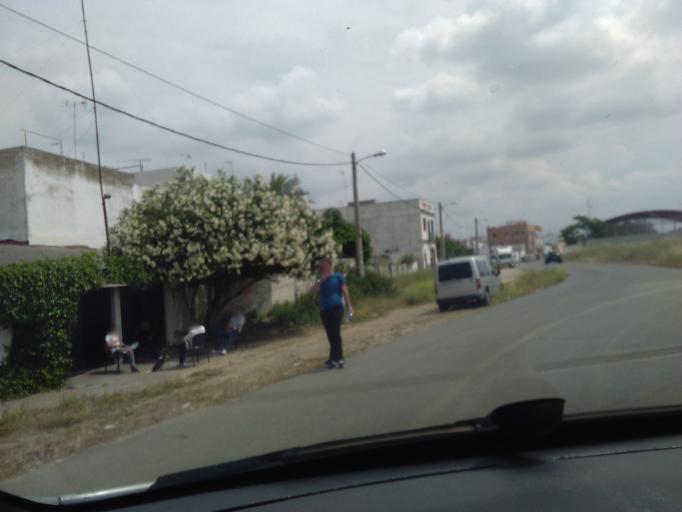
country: ES
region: Andalusia
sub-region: Provincia de Sevilla
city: Sevilla
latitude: 37.3664
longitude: -5.9479
